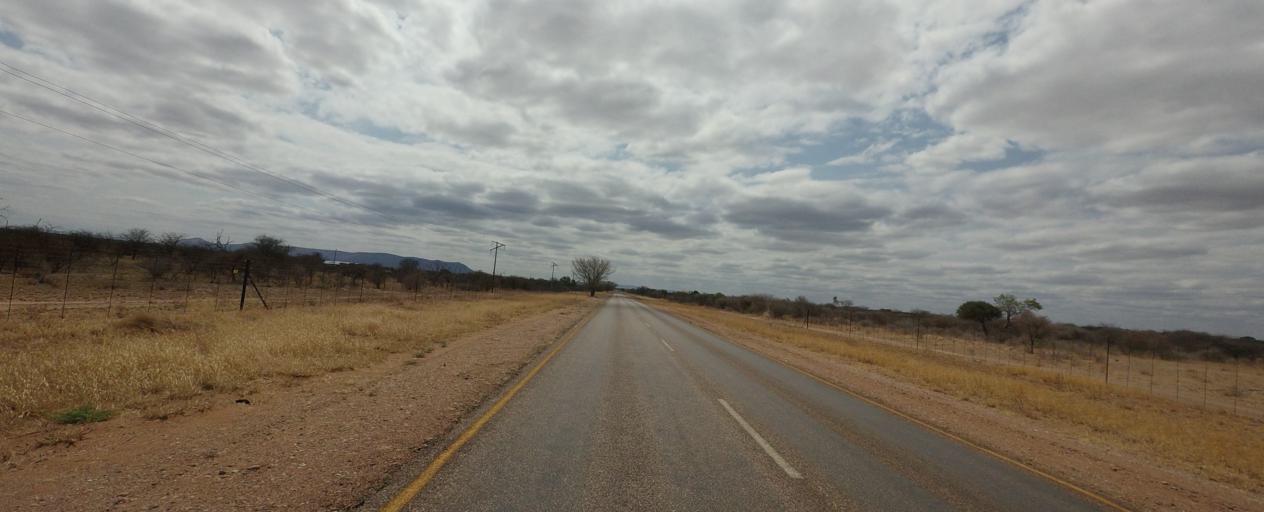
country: BW
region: Central
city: Makobeng
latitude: -23.0370
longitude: 27.9733
